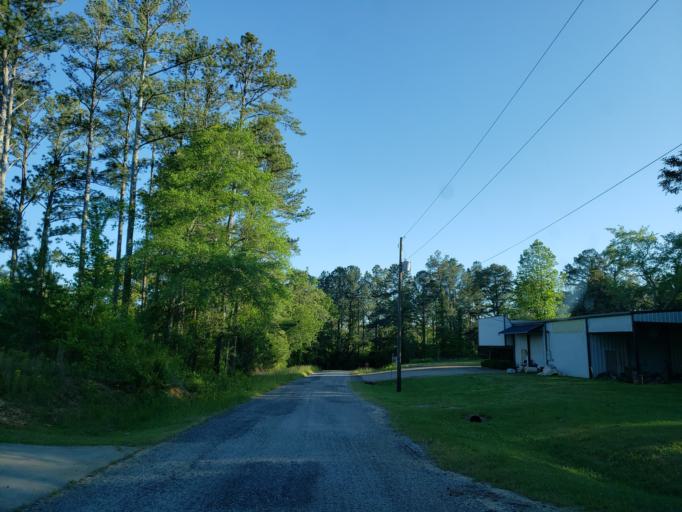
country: US
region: Georgia
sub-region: Haralson County
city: Tallapoosa
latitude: 33.7673
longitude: -85.3280
